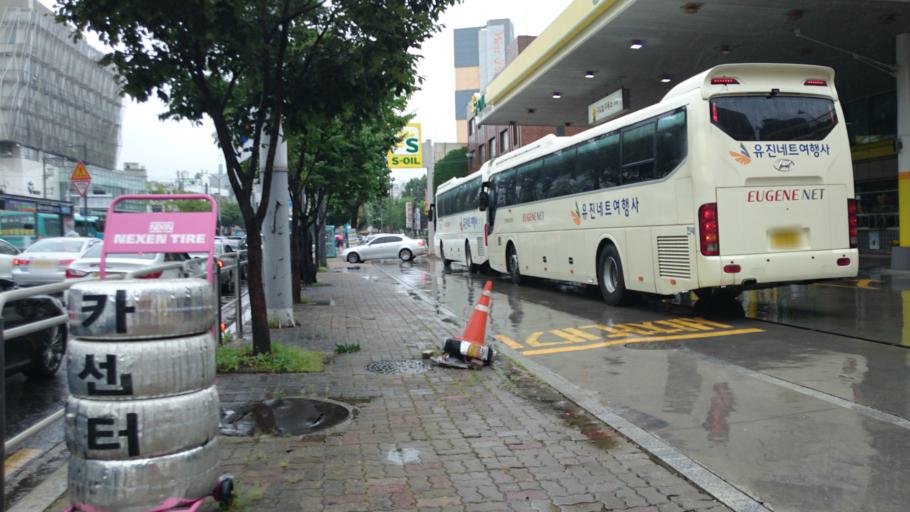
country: KR
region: Seoul
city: Seoul
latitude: 37.5663
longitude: 126.9247
